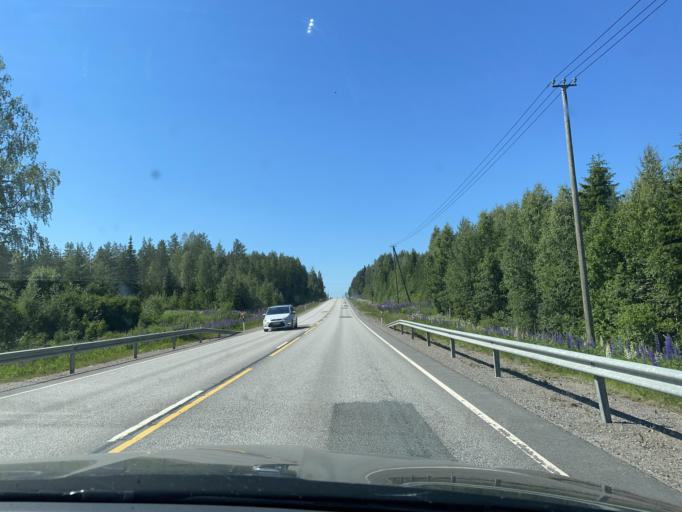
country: FI
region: Central Finland
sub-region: Saarijaervi-Viitasaari
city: Viitasaari
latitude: 63.1429
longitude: 25.7948
